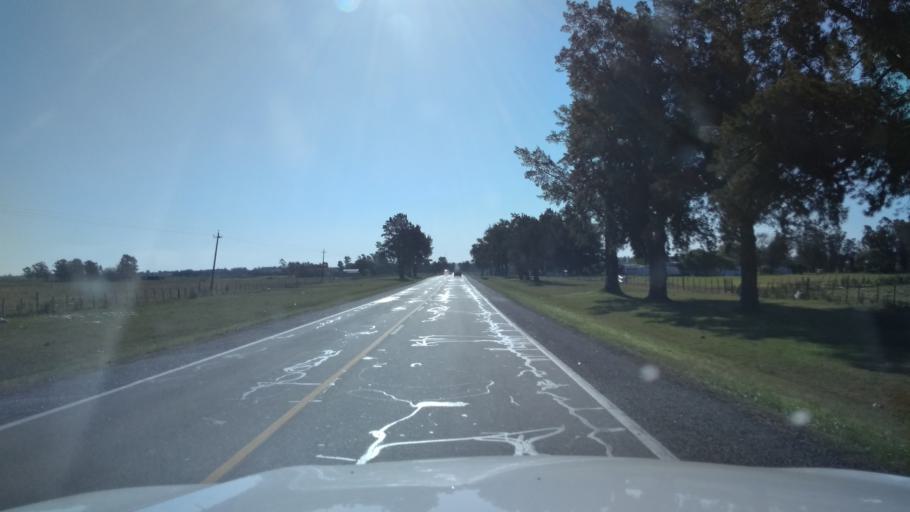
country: UY
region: Canelones
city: San Jacinto
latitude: -34.5769
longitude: -55.8473
